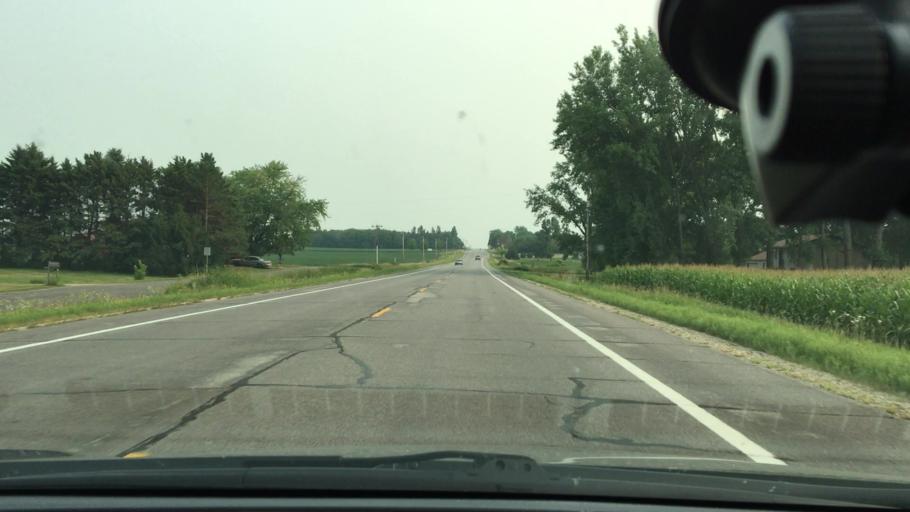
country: US
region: Minnesota
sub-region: Wright County
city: Albertville
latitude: 45.2608
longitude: -93.6634
